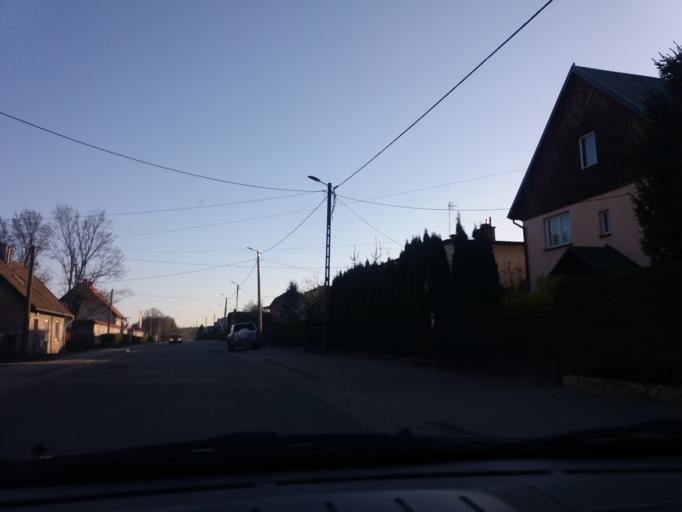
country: PL
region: Warmian-Masurian Voivodeship
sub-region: Powiat szczycienski
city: Szczytno
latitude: 53.5550
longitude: 20.9841
